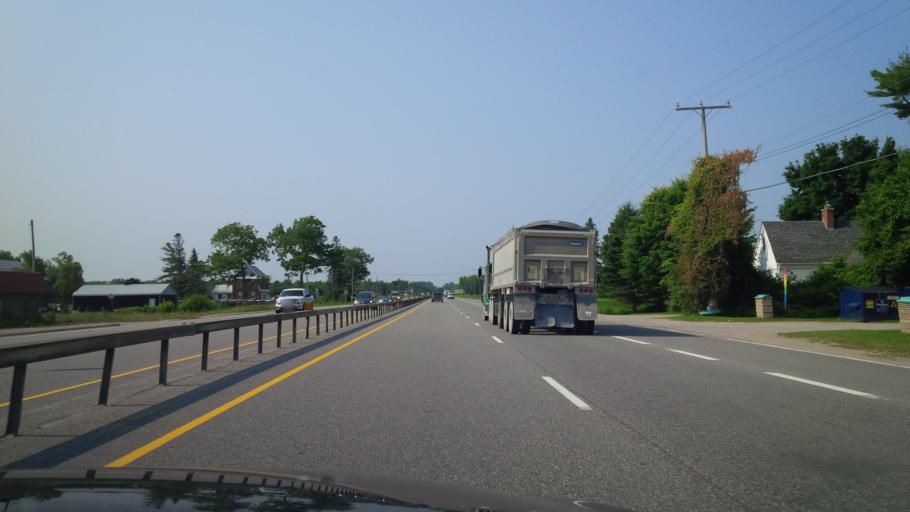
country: CA
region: Ontario
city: Orillia
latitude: 44.6863
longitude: -79.4032
